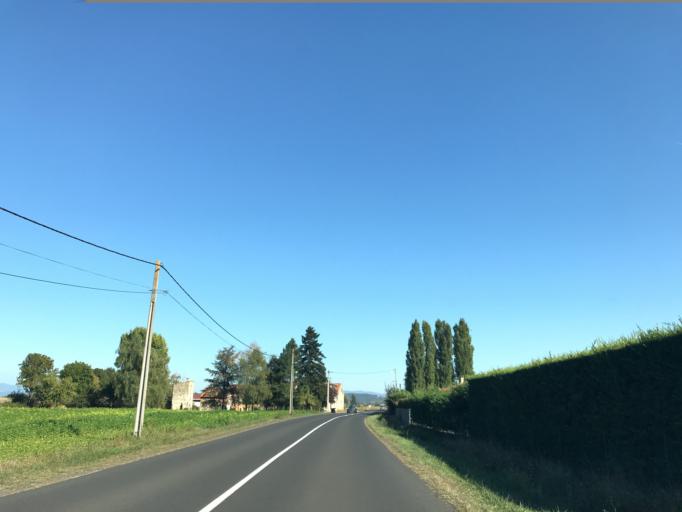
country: FR
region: Auvergne
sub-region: Departement du Puy-de-Dome
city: Vertaizon
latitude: 45.7829
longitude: 3.3116
